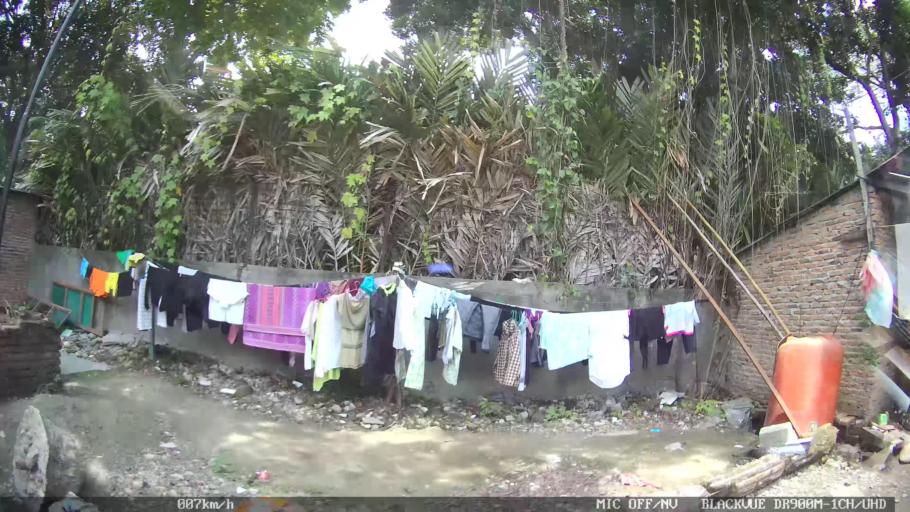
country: ID
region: North Sumatra
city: Medan
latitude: 3.6065
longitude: 98.7222
